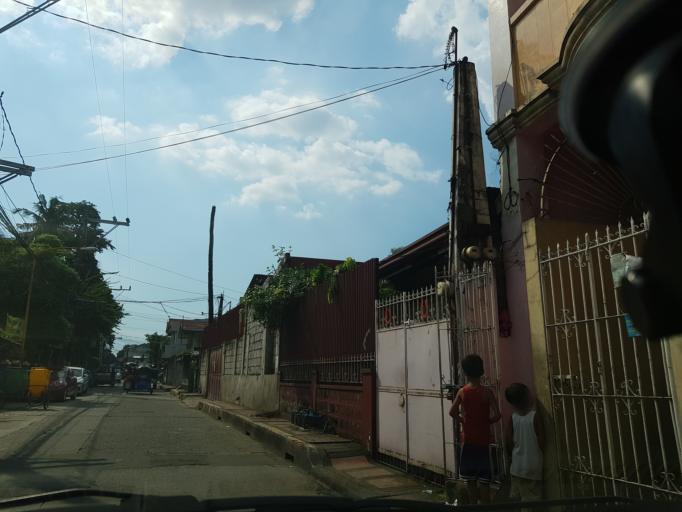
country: PH
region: Calabarzon
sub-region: Province of Rizal
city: Pateros
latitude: 14.5639
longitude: 121.0896
